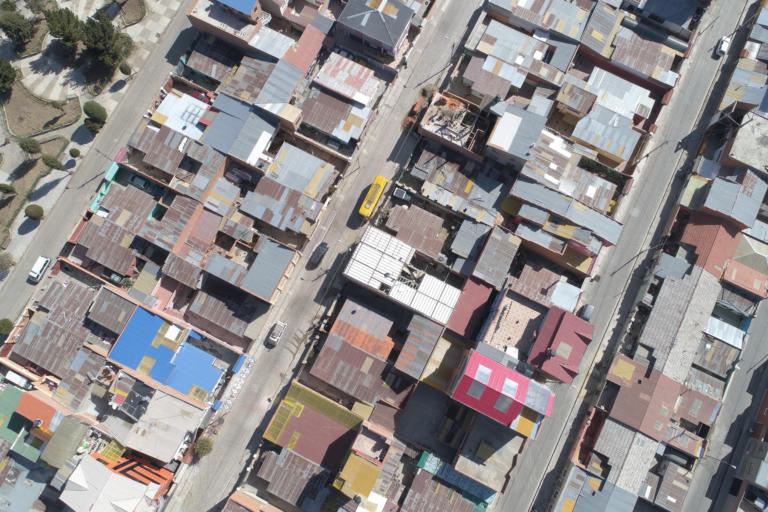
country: BO
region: La Paz
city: La Paz
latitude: -16.5291
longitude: -68.1542
